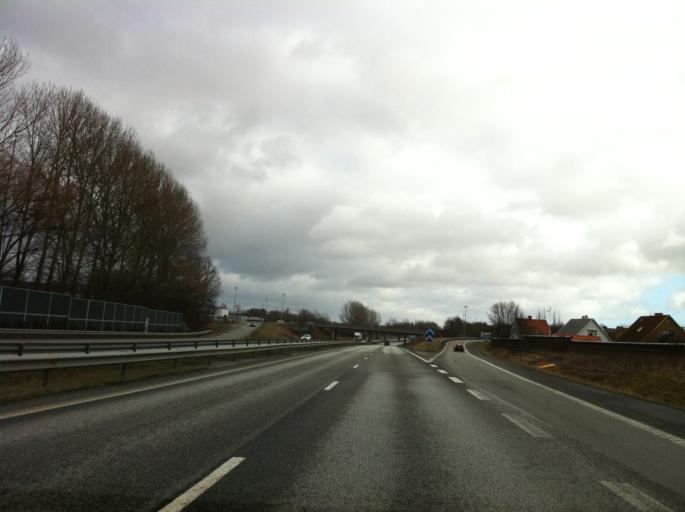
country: SE
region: Skane
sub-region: Kristianstads Kommun
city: Kristianstad
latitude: 56.0230
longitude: 14.1042
